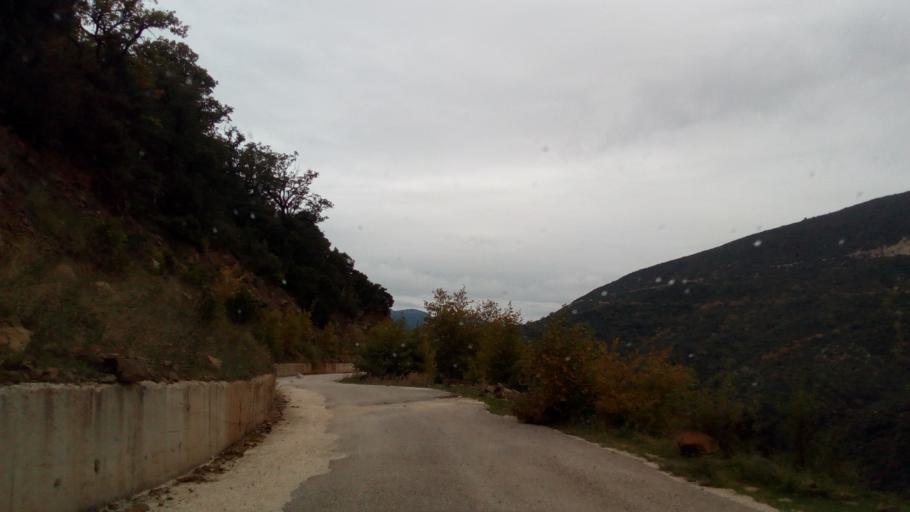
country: GR
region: West Greece
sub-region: Nomos Aitolias kai Akarnanias
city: Thermo
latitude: 38.6105
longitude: 21.8431
